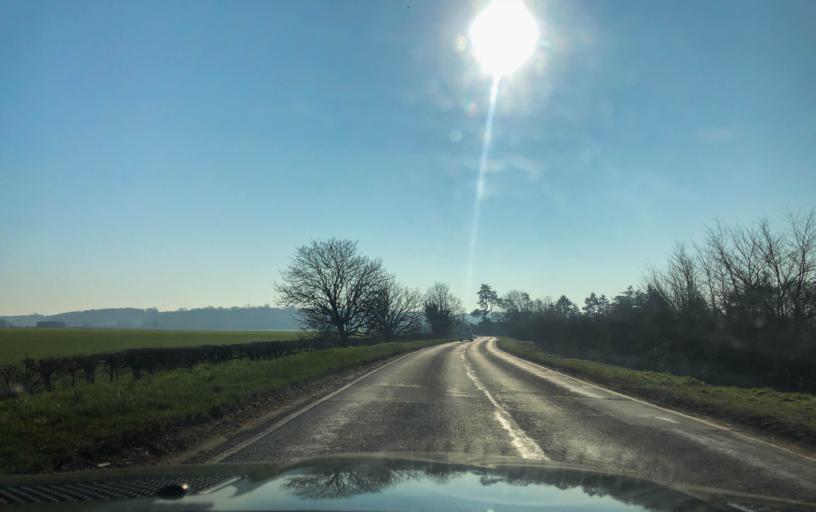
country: GB
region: England
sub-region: Warwickshire
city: Wellesbourne Mountford
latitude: 52.1901
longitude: -1.5845
